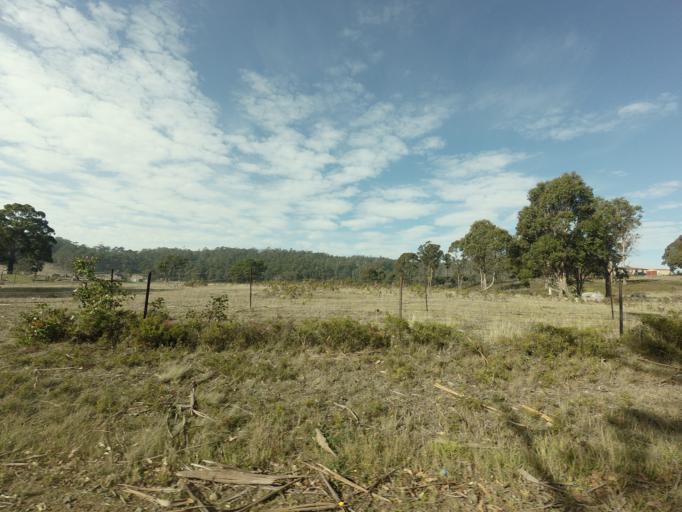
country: AU
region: Tasmania
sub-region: Sorell
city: Sorell
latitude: -42.4815
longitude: 147.4804
